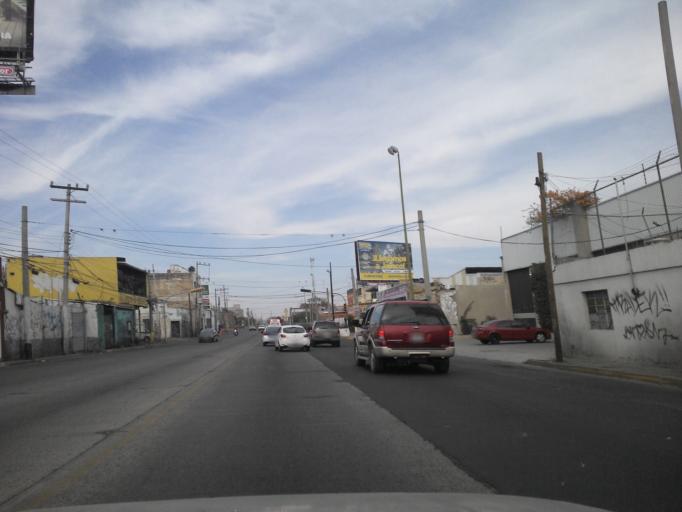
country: MX
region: Jalisco
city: Guadalajara
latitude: 20.6554
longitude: -103.3577
